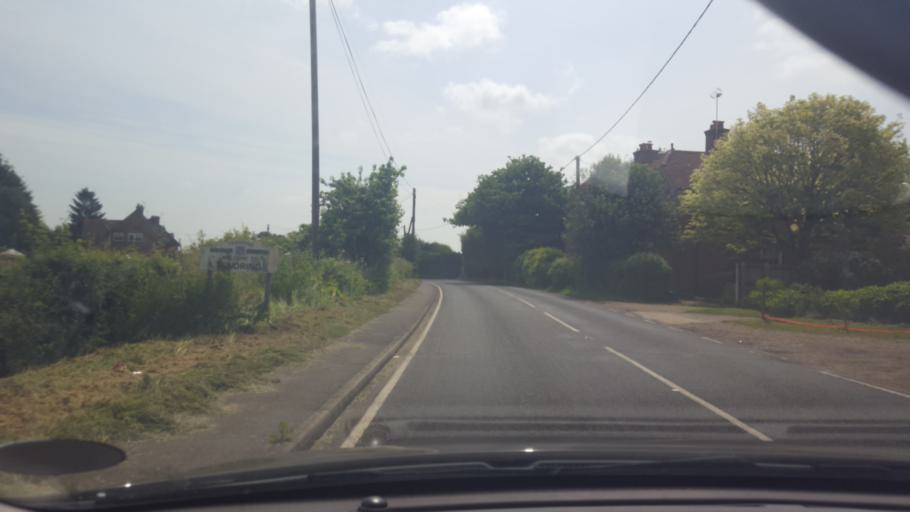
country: GB
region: England
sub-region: Essex
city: Great Bentley
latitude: 51.8843
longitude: 1.1104
